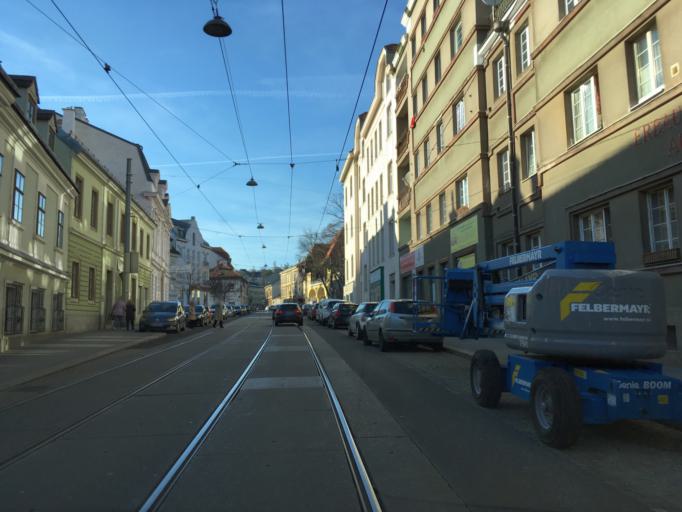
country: AT
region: Lower Austria
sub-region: Politischer Bezirk Wien-Umgebung
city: Klosterneuburg
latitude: 48.2314
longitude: 16.2946
